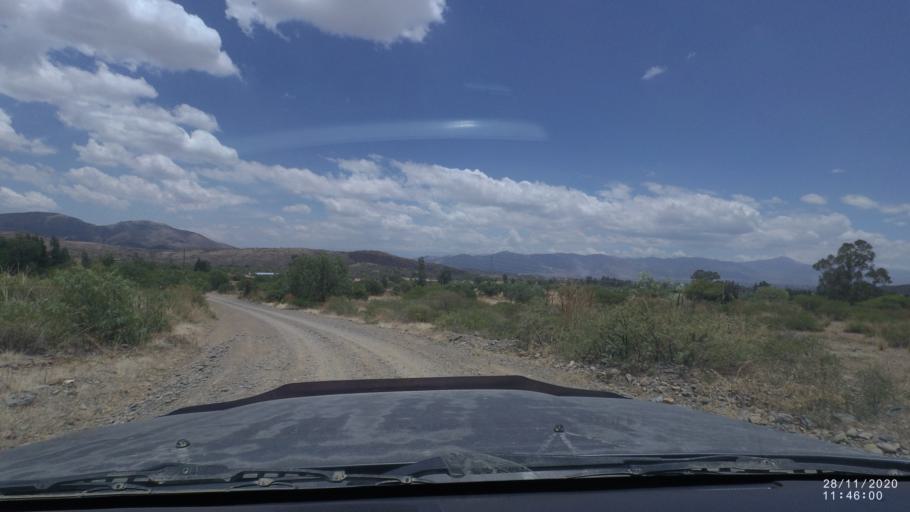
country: BO
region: Cochabamba
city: Tarata
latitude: -17.6534
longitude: -66.0426
